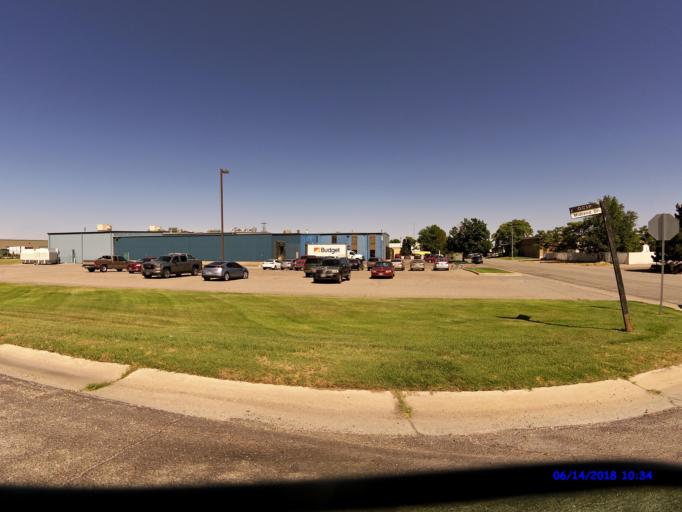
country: US
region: Utah
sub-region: Weber County
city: Riverdale
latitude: 41.2139
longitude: -112.0129
